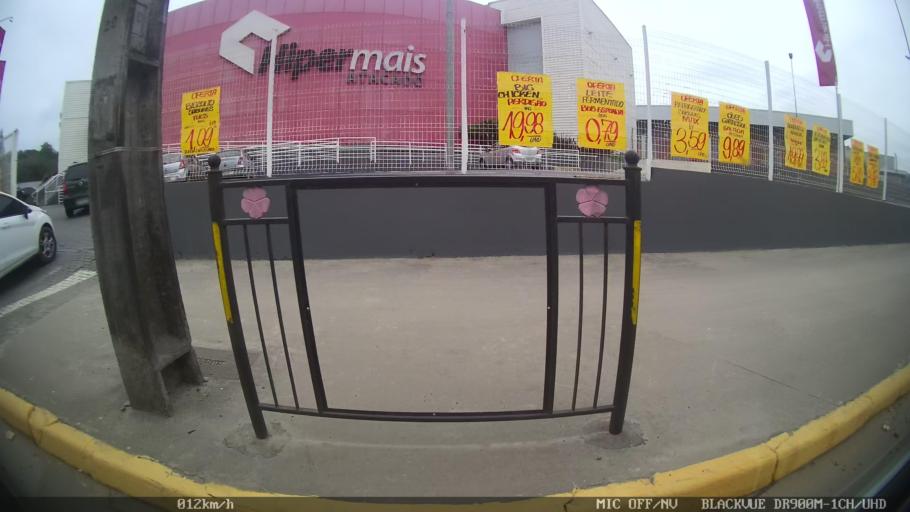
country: BR
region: Santa Catarina
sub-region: Joinville
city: Joinville
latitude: -26.3620
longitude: -48.8397
